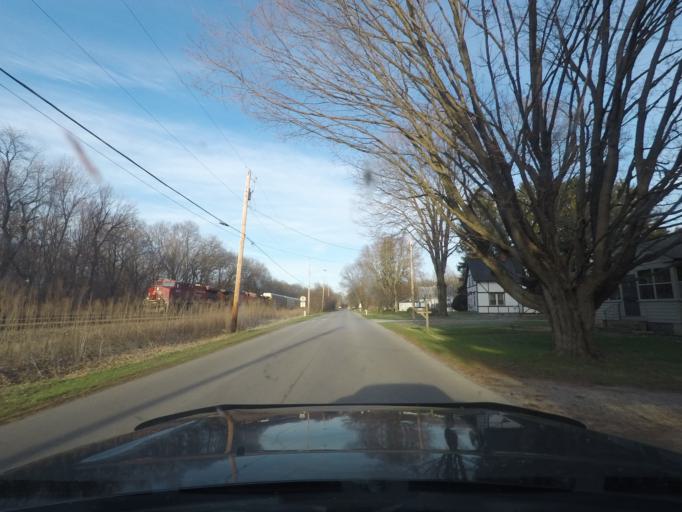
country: US
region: Indiana
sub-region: LaPorte County
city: LaPorte
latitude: 41.6044
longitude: -86.7466
